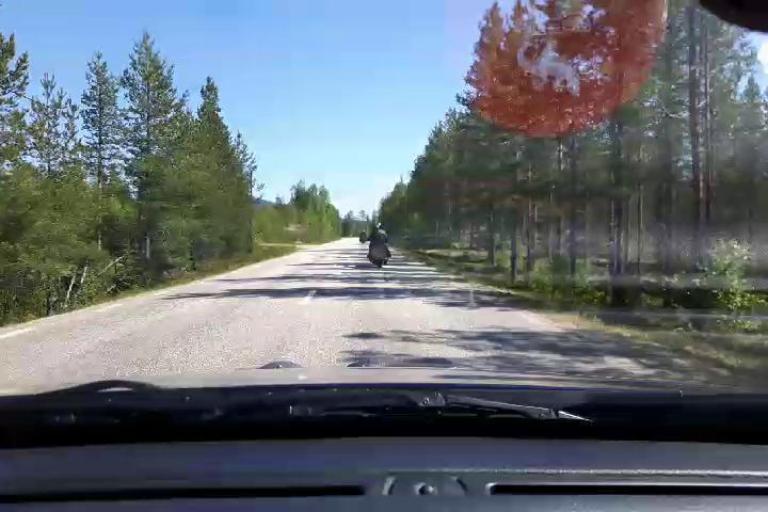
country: SE
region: Jaemtland
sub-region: Harjedalens Kommun
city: Sveg
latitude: 62.1236
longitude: 15.0056
